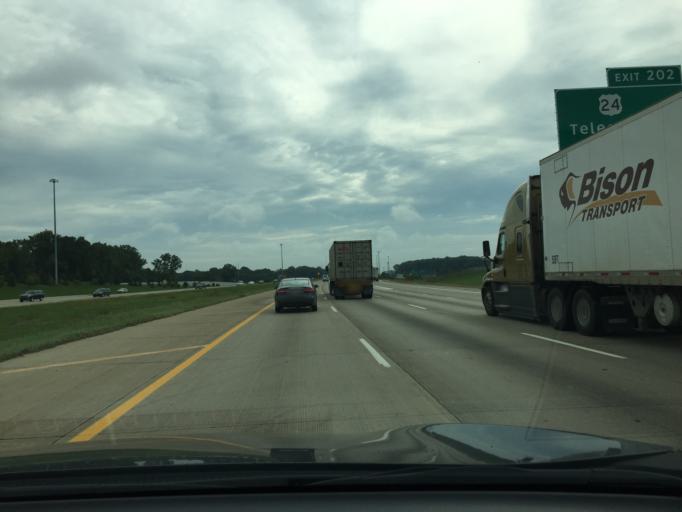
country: US
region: Michigan
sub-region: Wayne County
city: Taylor
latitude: 42.2642
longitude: -83.2786
